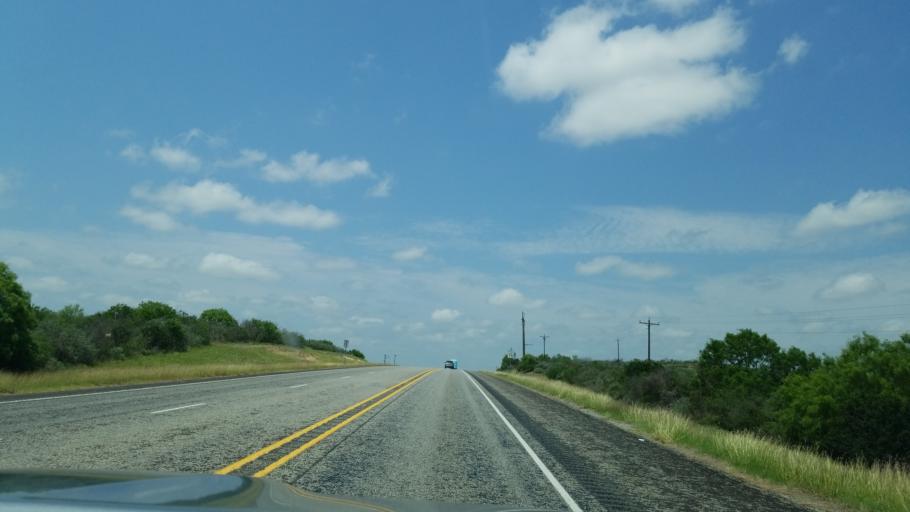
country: US
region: Texas
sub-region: Zavala County
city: Batesville
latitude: 28.9382
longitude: -99.7266
